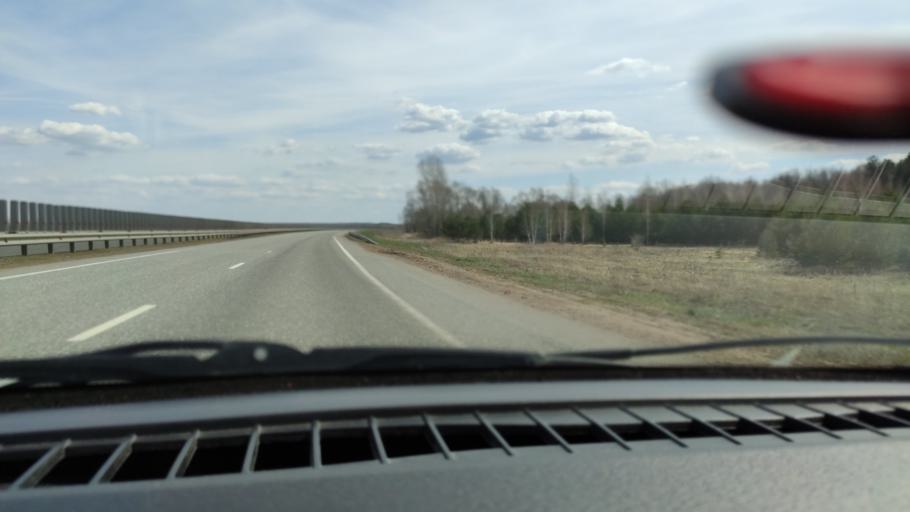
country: RU
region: Bashkortostan
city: Kushnarenkovo
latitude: 55.0649
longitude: 55.3672
